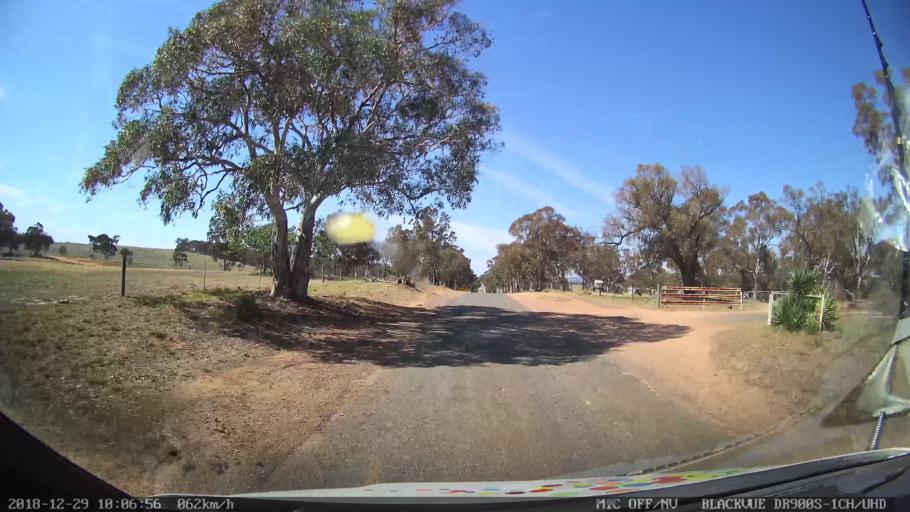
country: AU
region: New South Wales
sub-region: Yass Valley
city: Gundaroo
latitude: -34.8479
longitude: 149.4542
